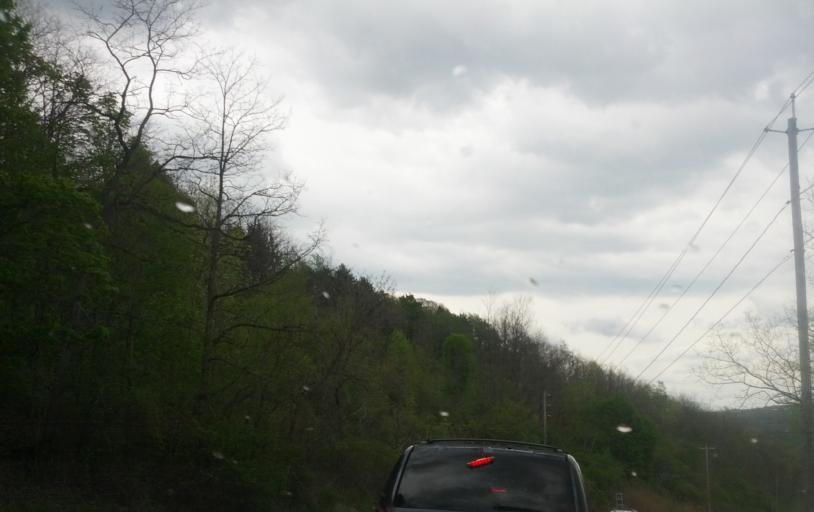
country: US
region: New York
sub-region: Onondaga County
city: Nedrow
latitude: 43.0055
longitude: -76.1653
